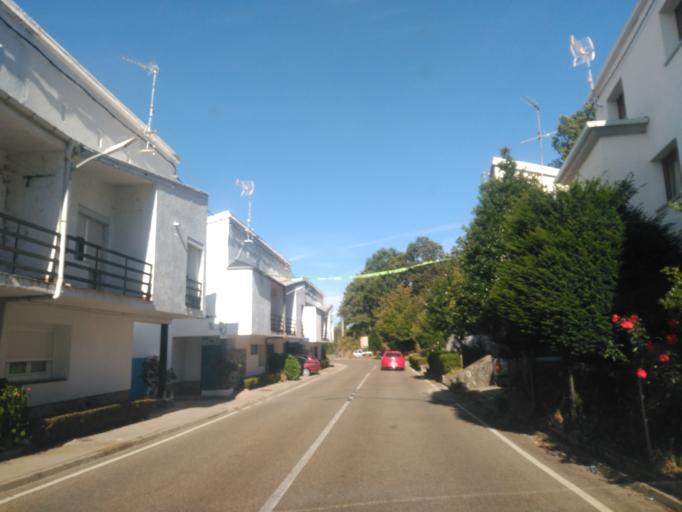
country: ES
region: Castille and Leon
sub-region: Provincia de Zamora
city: Cobreros
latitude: 42.1146
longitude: -6.7380
